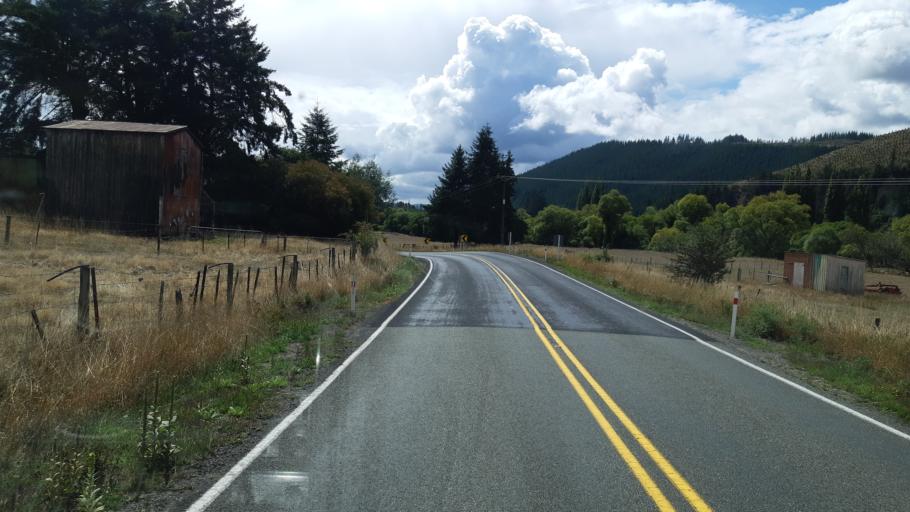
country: NZ
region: Tasman
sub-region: Tasman District
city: Wakefield
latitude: -41.4806
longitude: 172.8014
